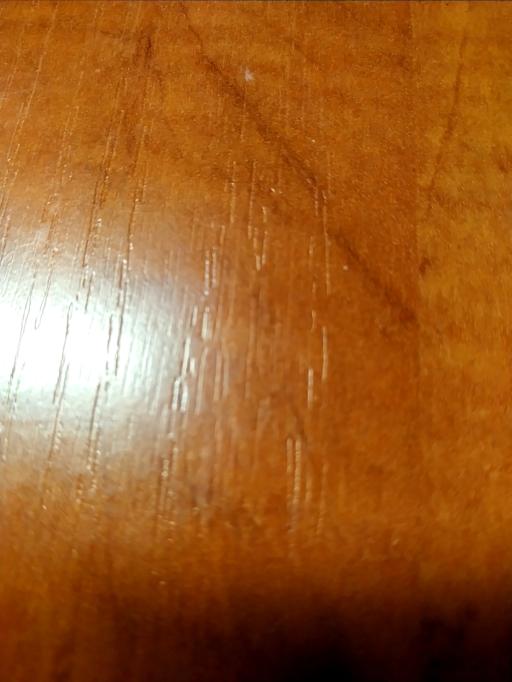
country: RU
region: Kaluga
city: Iznoski
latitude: 55.0138
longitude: 35.4042
